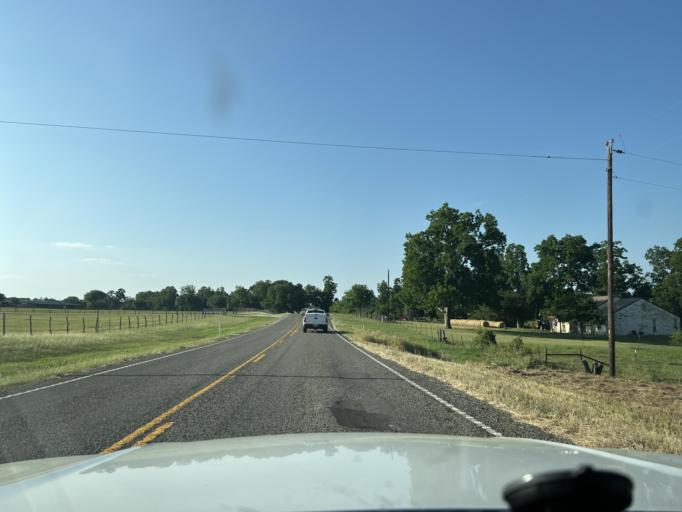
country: US
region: Texas
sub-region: Washington County
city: Brenham
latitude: 30.2263
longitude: -96.2382
